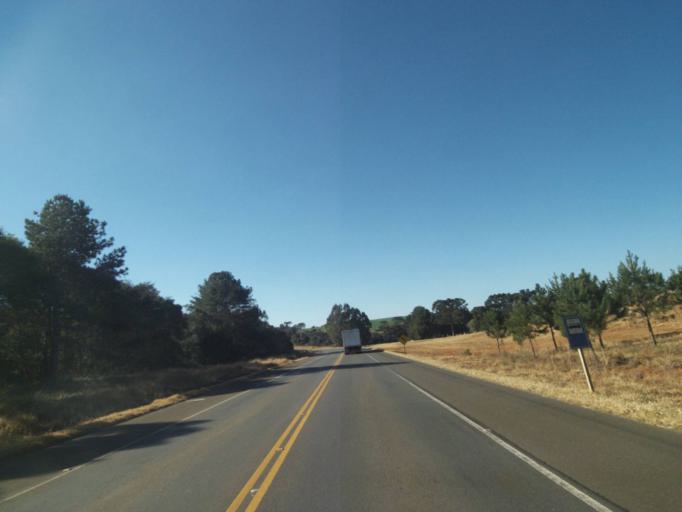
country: BR
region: Parana
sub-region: Tibagi
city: Tibagi
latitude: -24.5501
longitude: -50.4540
